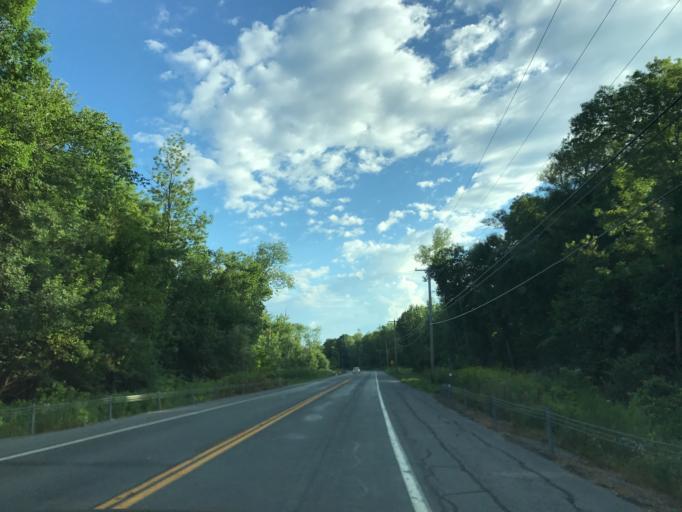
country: US
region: New York
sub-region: Saratoga County
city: Schuylerville
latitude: 43.1443
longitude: -73.5815
